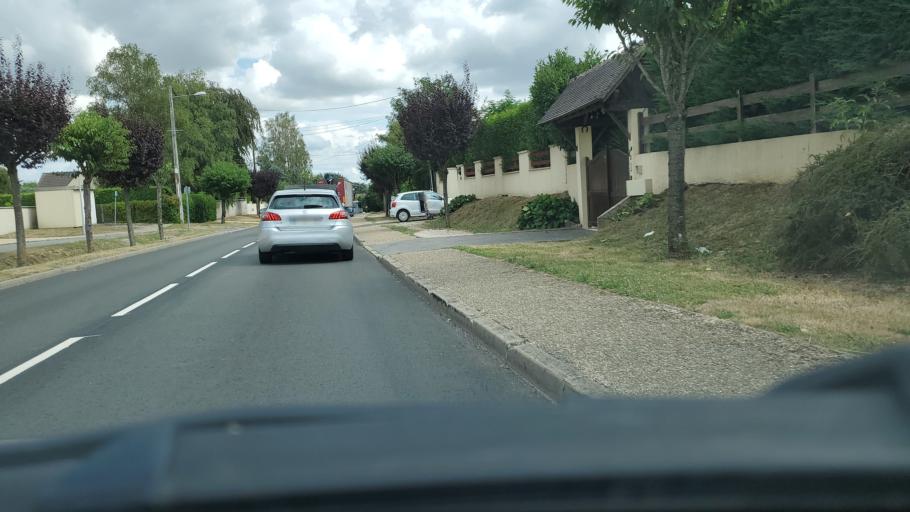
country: FR
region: Ile-de-France
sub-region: Departement de Seine-et-Marne
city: La Chapelle-sur-Crecy
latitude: 48.8880
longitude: 2.9573
